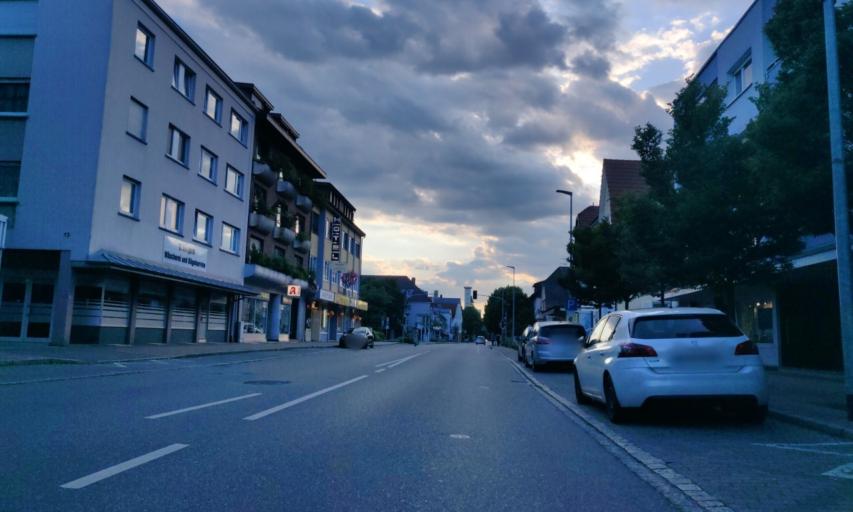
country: CH
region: Basel-City
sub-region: Basel-Stadt
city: Bettingen
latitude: 47.5530
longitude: 7.6603
